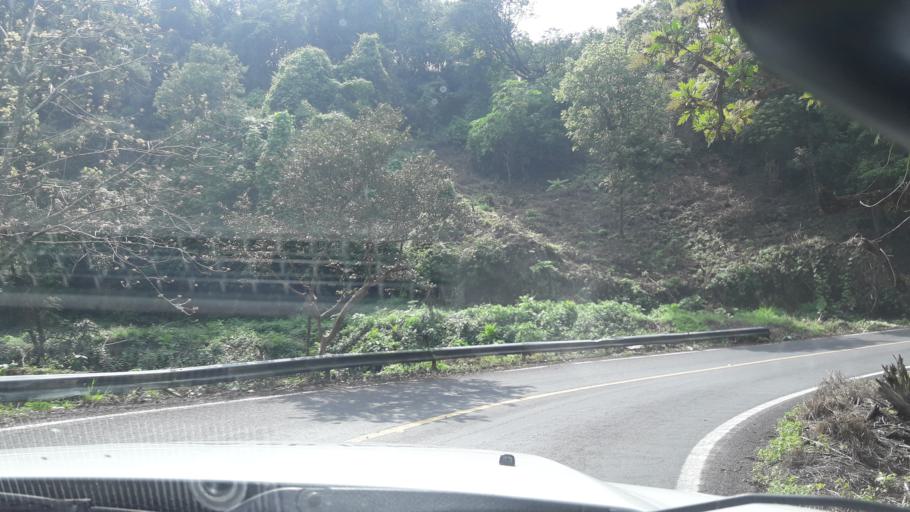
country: MX
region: Colima
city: Suchitlan
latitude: 19.4298
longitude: -103.6977
